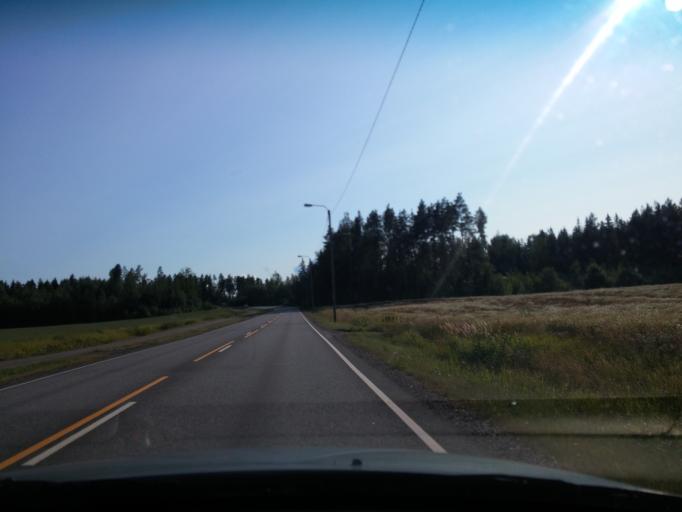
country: FI
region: Uusimaa
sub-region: Porvoo
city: Askola
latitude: 60.5070
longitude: 25.5688
